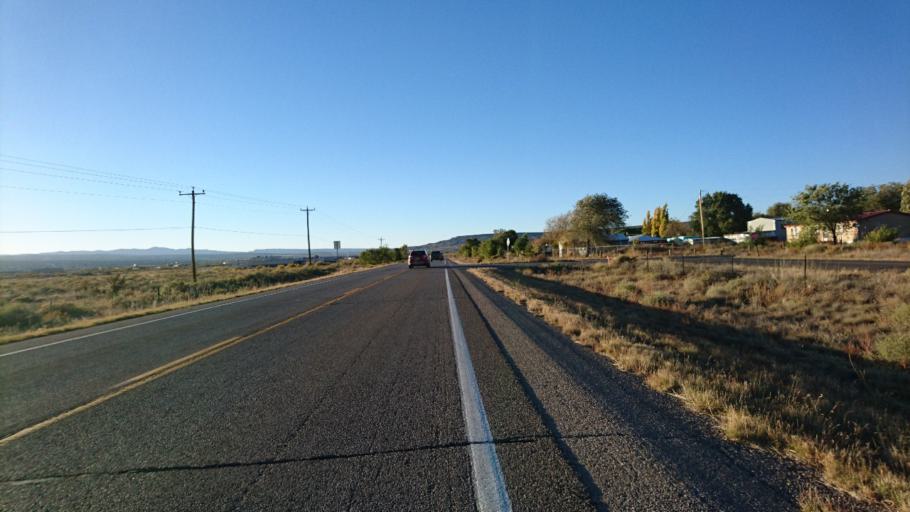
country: US
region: New Mexico
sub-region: Cibola County
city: Grants
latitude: 35.1279
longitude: -107.8063
